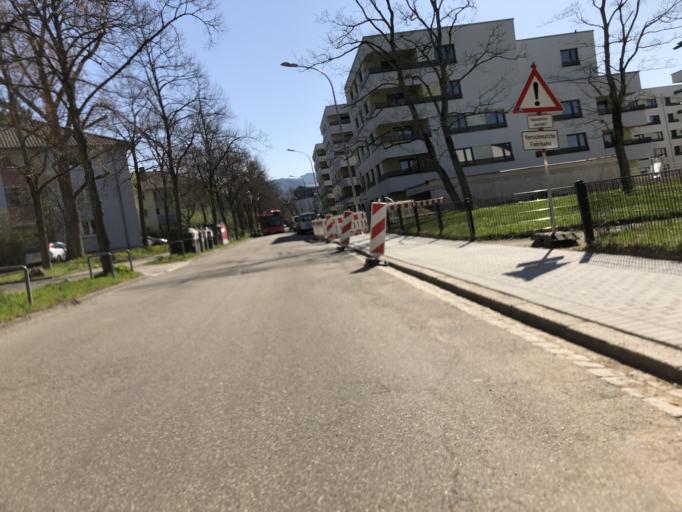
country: DE
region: Baden-Wuerttemberg
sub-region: Freiburg Region
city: Merzhausen
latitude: 47.9879
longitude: 7.8149
